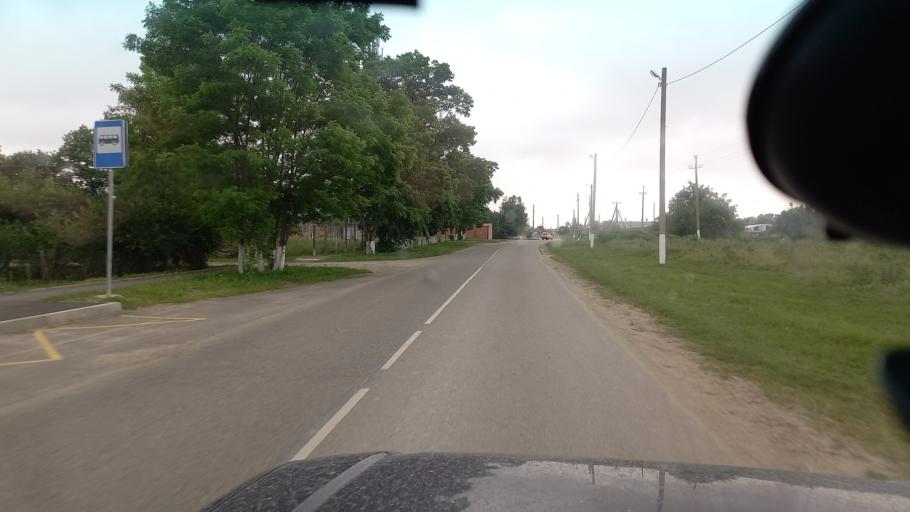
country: RU
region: Krasnodarskiy
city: Mostovskoy
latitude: 44.4225
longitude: 40.7753
